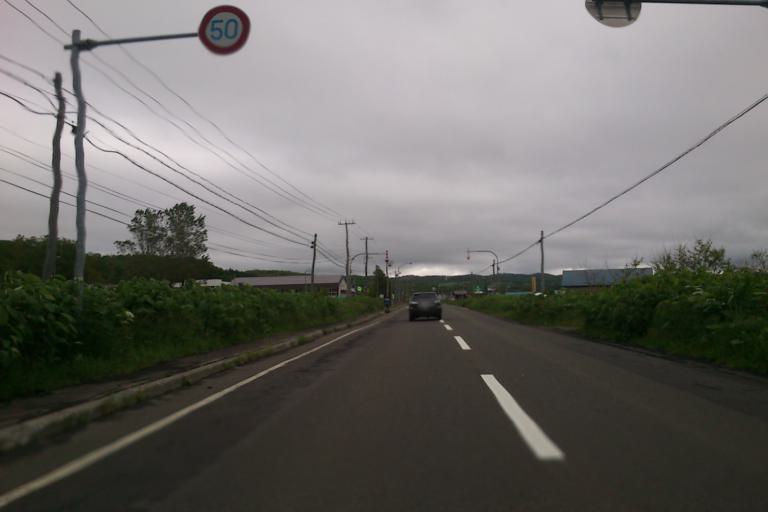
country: JP
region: Hokkaido
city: Ishikari
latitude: 43.3170
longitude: 141.4256
